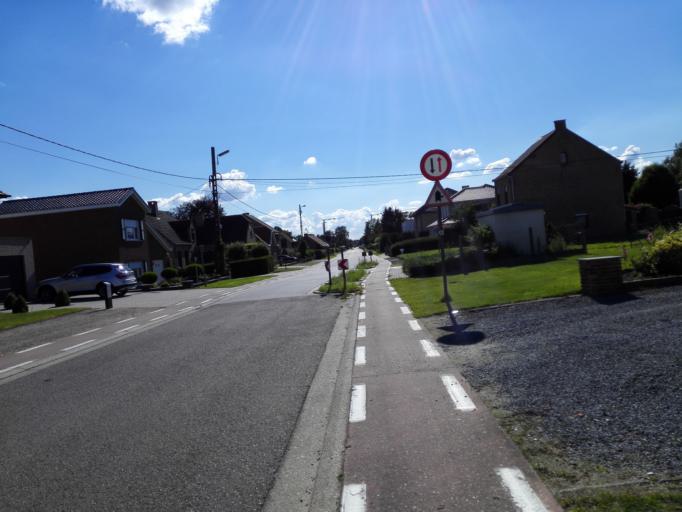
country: BE
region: Flanders
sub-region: Provincie Vlaams-Brabant
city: Begijnendijk
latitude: 50.9858
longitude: 4.7658
